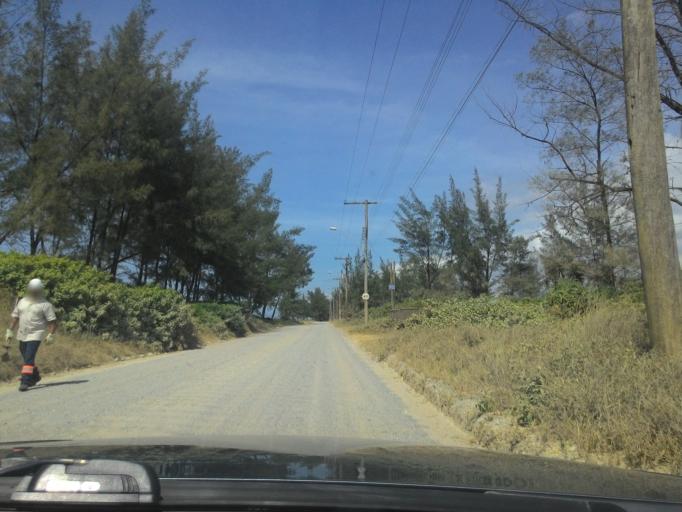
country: BR
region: Sao Paulo
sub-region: Iguape
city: Iguape
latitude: -24.8392
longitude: -47.6798
